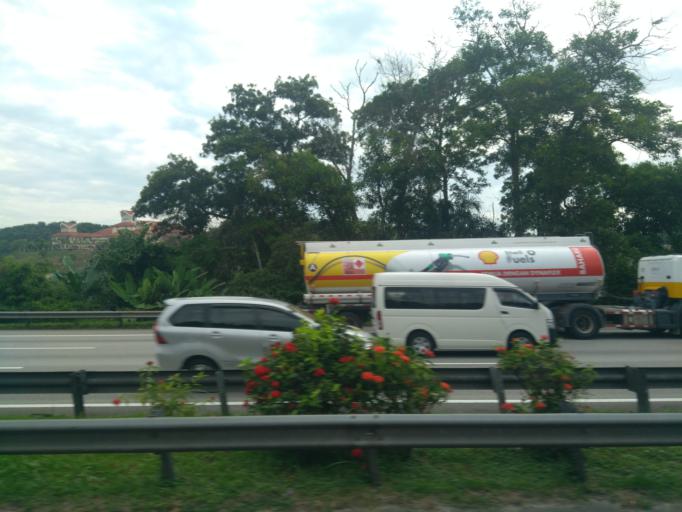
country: MY
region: Negeri Sembilan
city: Seremban
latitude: 2.6469
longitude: 101.9925
